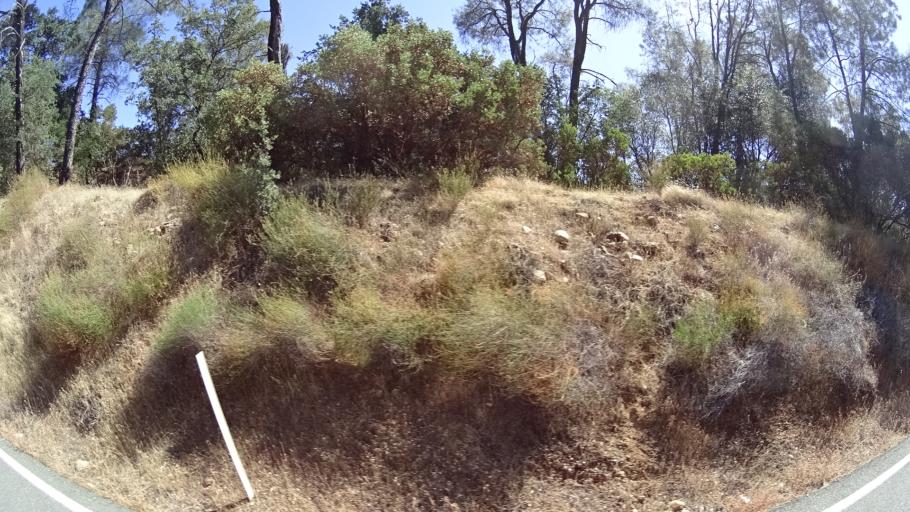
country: US
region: California
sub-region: Calaveras County
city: Valley Springs
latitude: 38.2252
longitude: -120.8859
